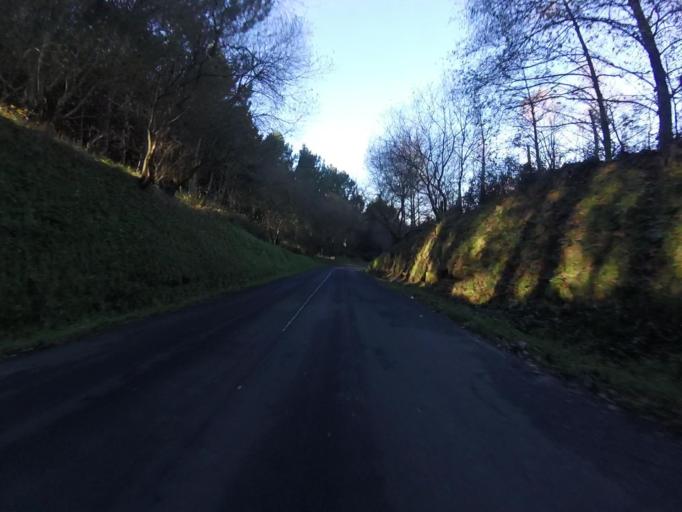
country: ES
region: Basque Country
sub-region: Provincia de Guipuzcoa
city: Fuenterrabia
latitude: 43.3656
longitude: -1.8304
